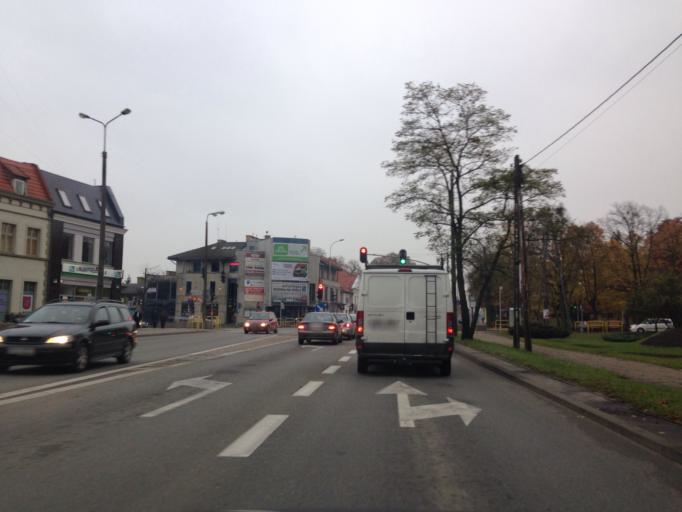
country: PL
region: Pomeranian Voivodeship
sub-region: Powiat gdanski
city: Pruszcz Gdanski
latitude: 54.2629
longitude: 18.6361
